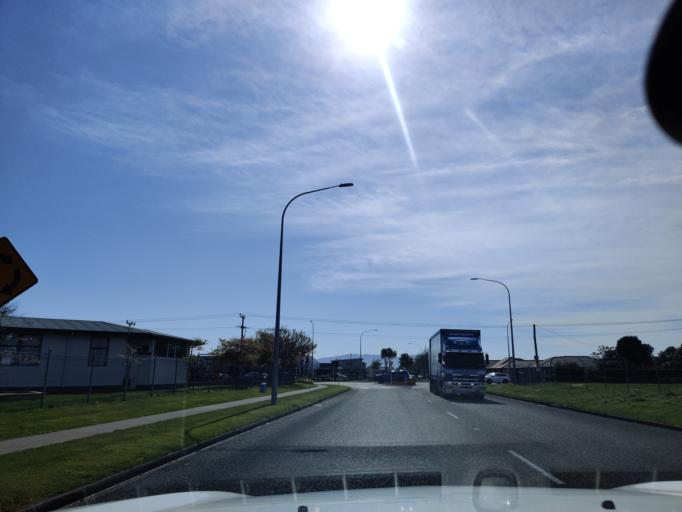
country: NZ
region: Manawatu-Wanganui
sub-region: Palmerston North City
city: Palmerston North
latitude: -40.3310
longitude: 175.6514
